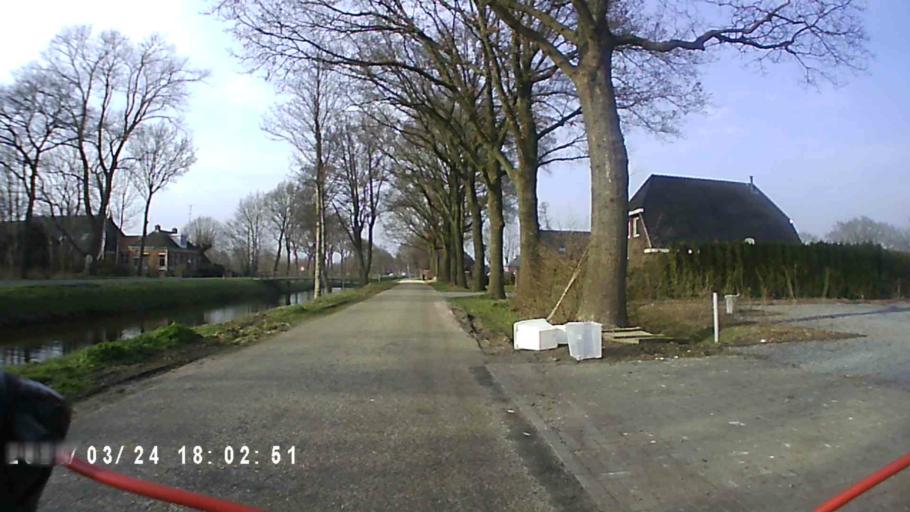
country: NL
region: Groningen
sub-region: Gemeente Leek
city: Leek
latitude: 53.1409
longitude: 6.3598
